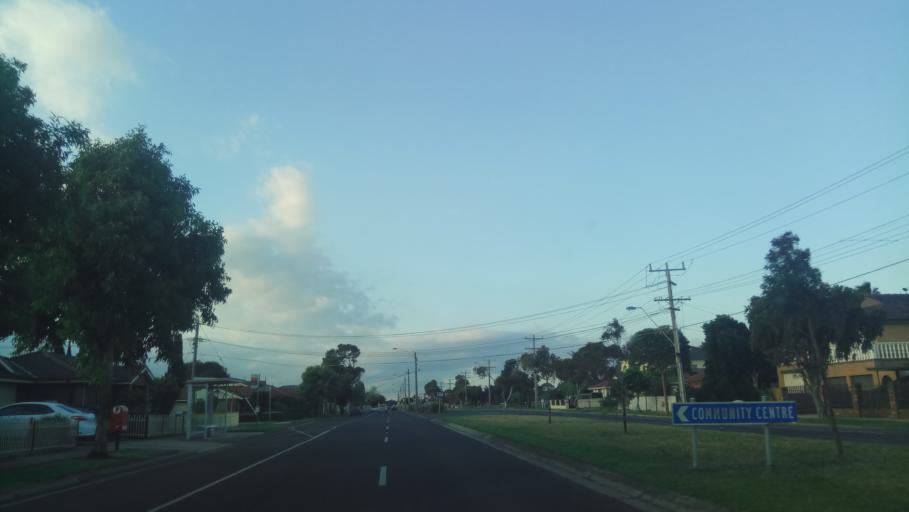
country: AU
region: Victoria
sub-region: Hobsons Bay
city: Altona Meadows
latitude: -37.8783
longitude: 144.7858
